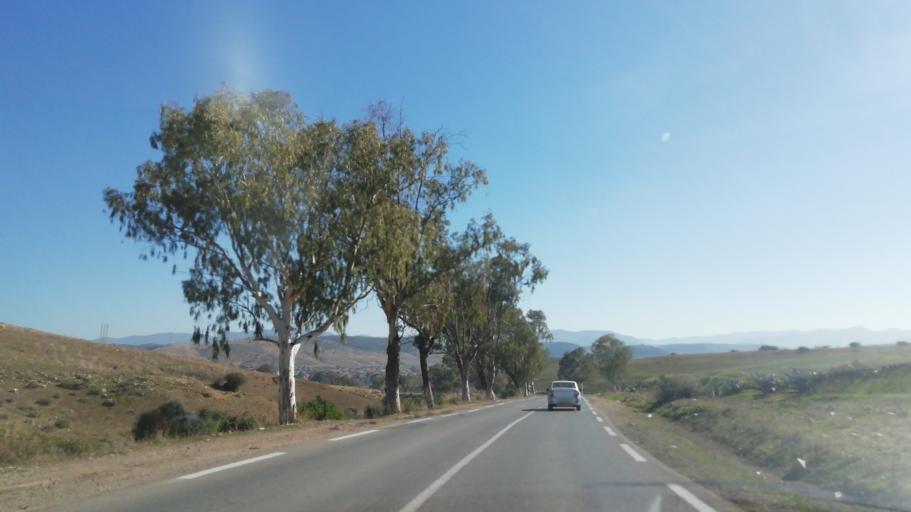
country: DZ
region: Tlemcen
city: Nedroma
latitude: 34.8299
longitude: -1.6650
